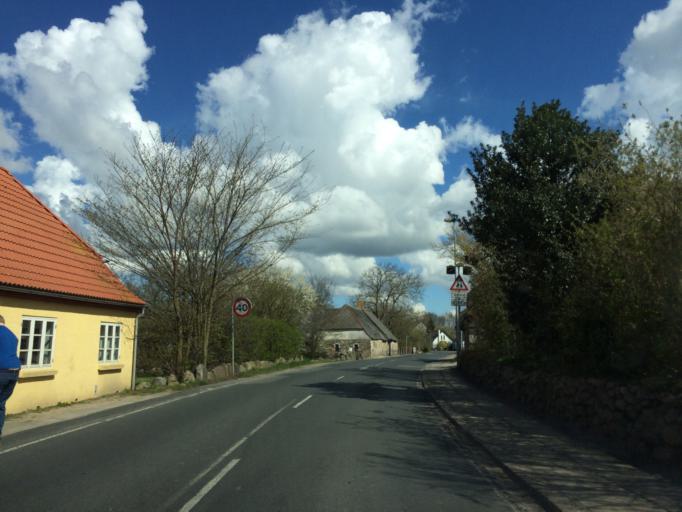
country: DK
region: South Denmark
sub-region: Assens Kommune
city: Harby
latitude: 55.2006
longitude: 10.1562
